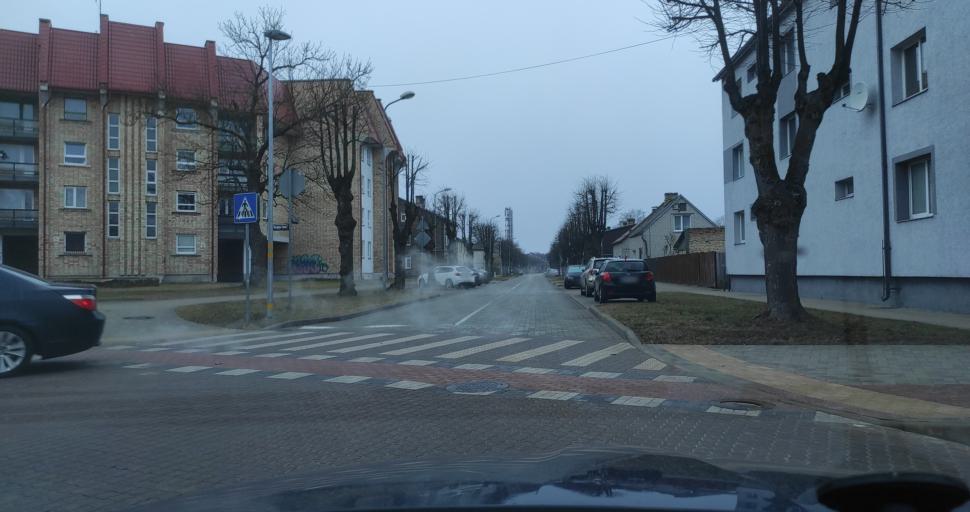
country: LV
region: Ventspils
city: Ventspils
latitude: 57.3884
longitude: 21.5581
